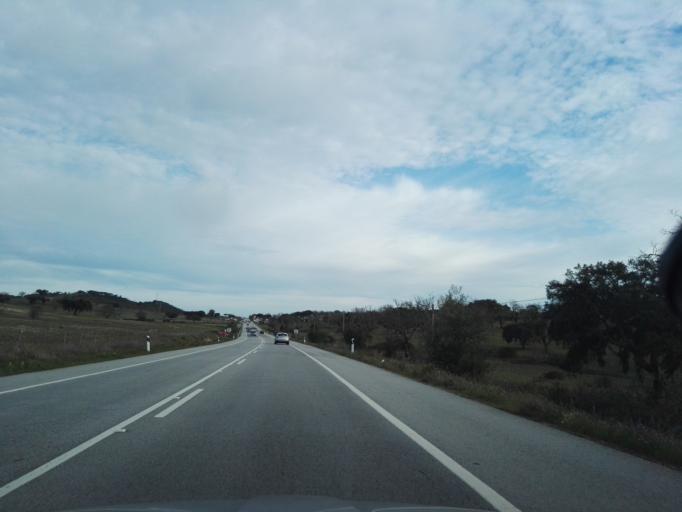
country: PT
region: Portalegre
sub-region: Portalegre
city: Urra
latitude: 39.2474
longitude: -7.4018
